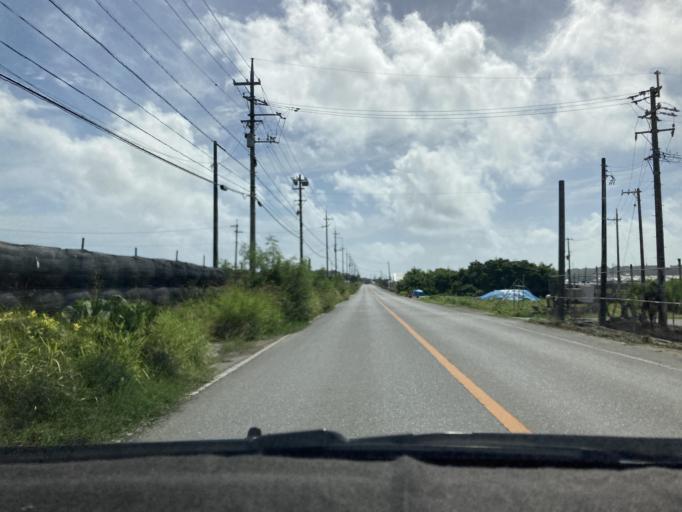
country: JP
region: Okinawa
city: Itoman
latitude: 26.1027
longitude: 127.6702
